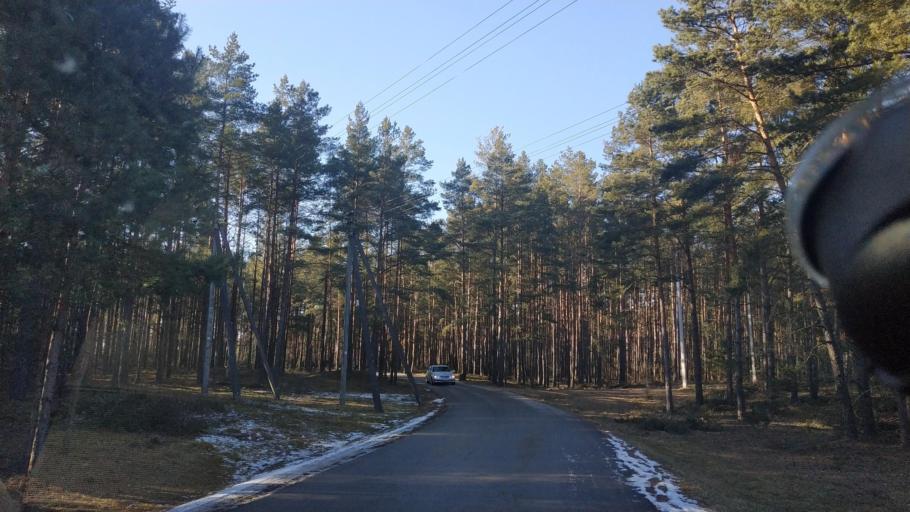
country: LT
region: Alytaus apskritis
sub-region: Alytaus rajonas
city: Daugai
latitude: 54.1628
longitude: 24.1780
